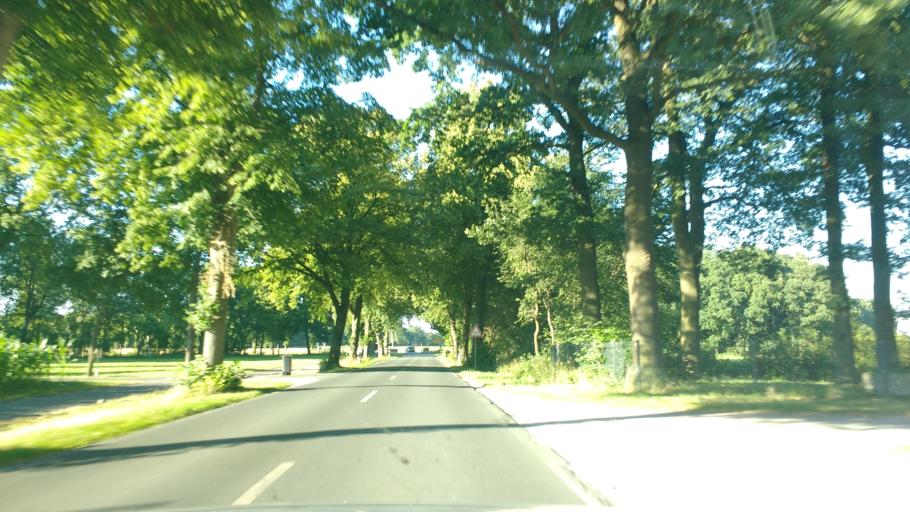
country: DE
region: North Rhine-Westphalia
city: Rietberg
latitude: 51.7166
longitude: 8.4382
